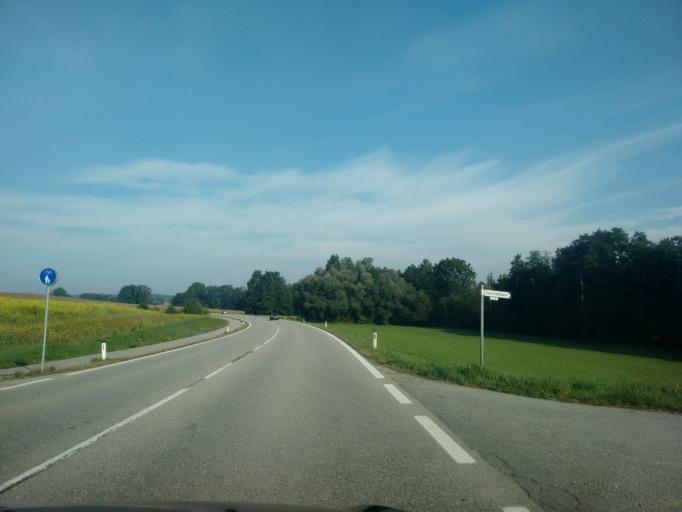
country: AT
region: Upper Austria
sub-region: Politischer Bezirk Grieskirchen
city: Grieskirchen
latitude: 48.2581
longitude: 13.7631
